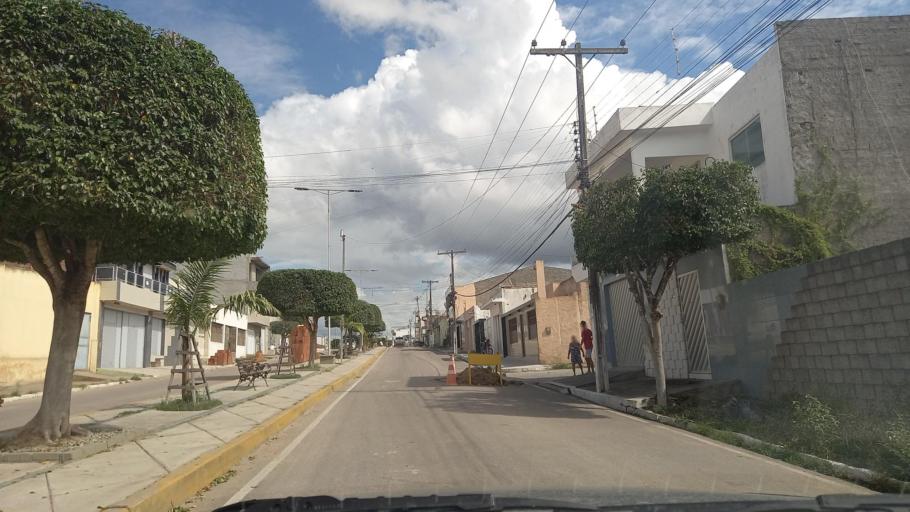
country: BR
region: Pernambuco
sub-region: Cachoeirinha
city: Cachoeirinha
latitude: -8.4904
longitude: -36.2378
